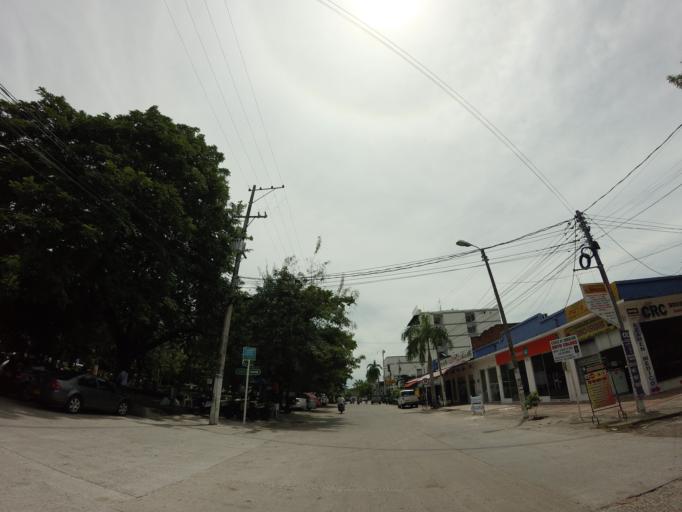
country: CO
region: Caldas
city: La Dorada
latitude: 5.4541
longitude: -74.6628
